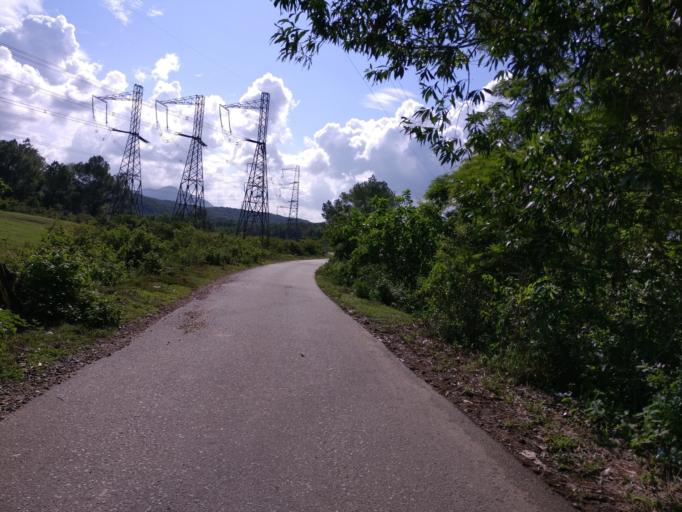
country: VN
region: Thua Thien-Hue
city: Hue
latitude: 16.4062
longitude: 107.5914
